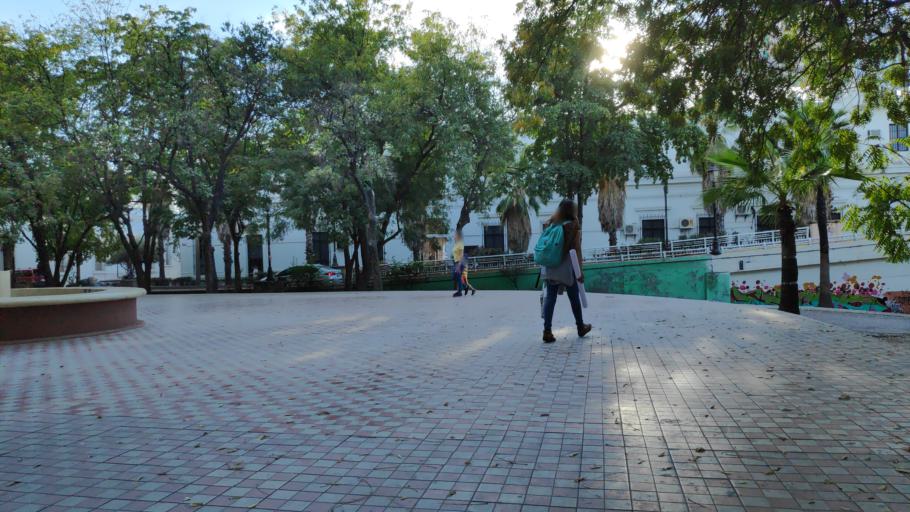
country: MX
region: Sinaloa
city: Culiacan
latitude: 24.8096
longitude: -107.4017
